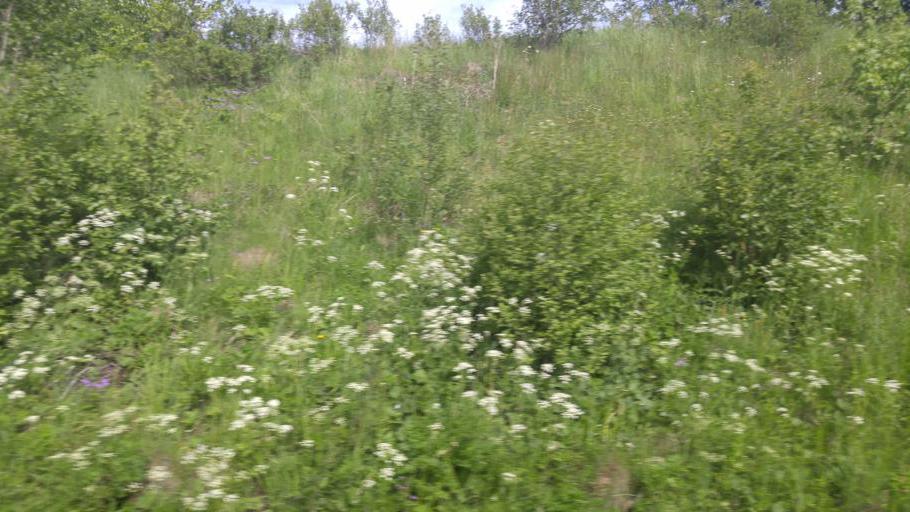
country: NO
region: Sor-Trondelag
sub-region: Trondheim
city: Trondheim
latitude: 63.3852
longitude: 10.3586
